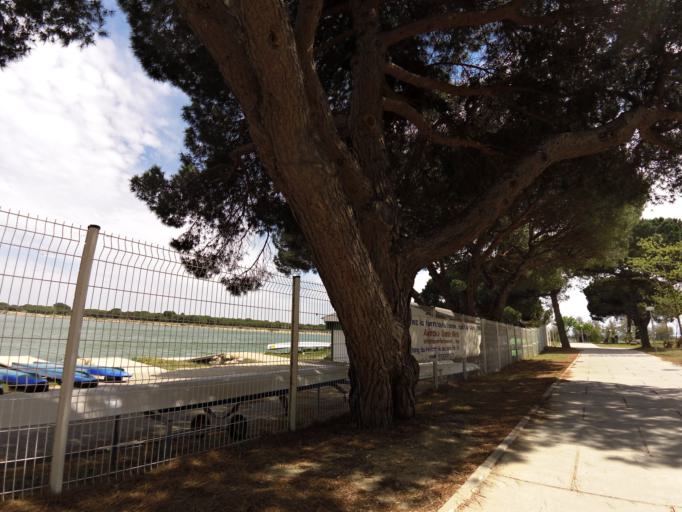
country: FR
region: Languedoc-Roussillon
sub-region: Departement de l'Herault
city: La Grande-Motte
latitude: 43.5589
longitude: 4.1008
